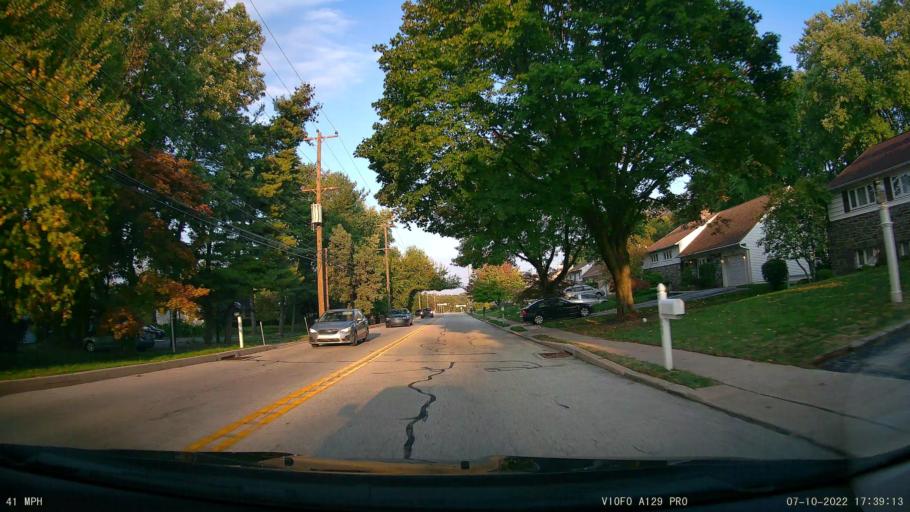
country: US
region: Pennsylvania
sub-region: Montgomery County
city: King of Prussia
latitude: 40.1029
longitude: -75.3875
